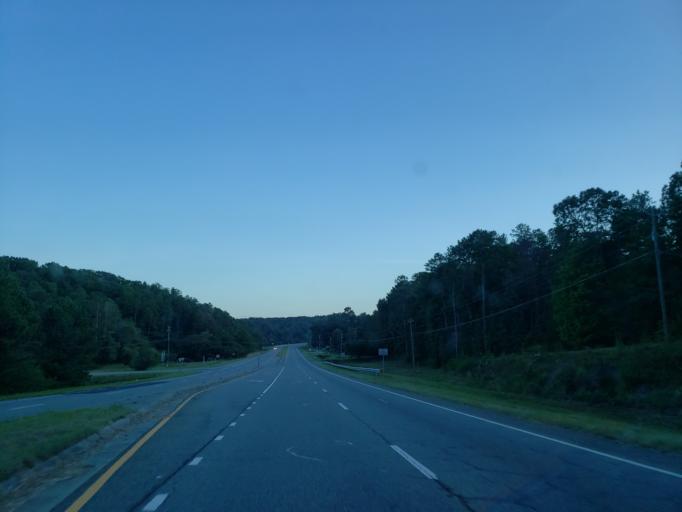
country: US
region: Georgia
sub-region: Floyd County
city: Lindale
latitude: 34.1350
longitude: -85.2161
